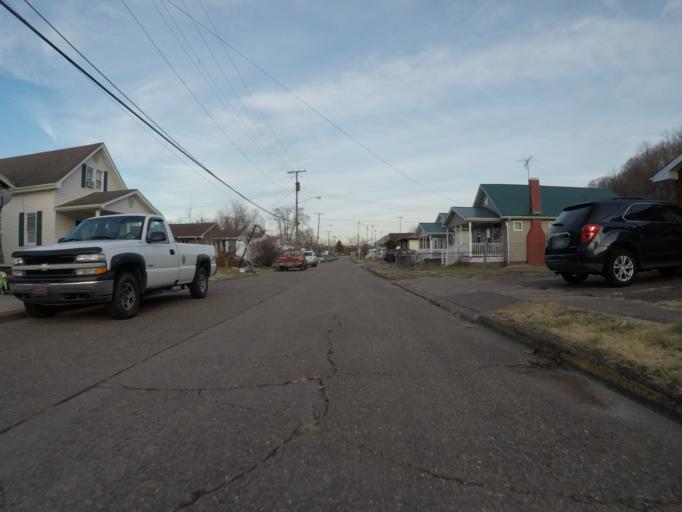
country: US
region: Ohio
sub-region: Lawrence County
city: Burlington
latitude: 38.3975
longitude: -82.5153
